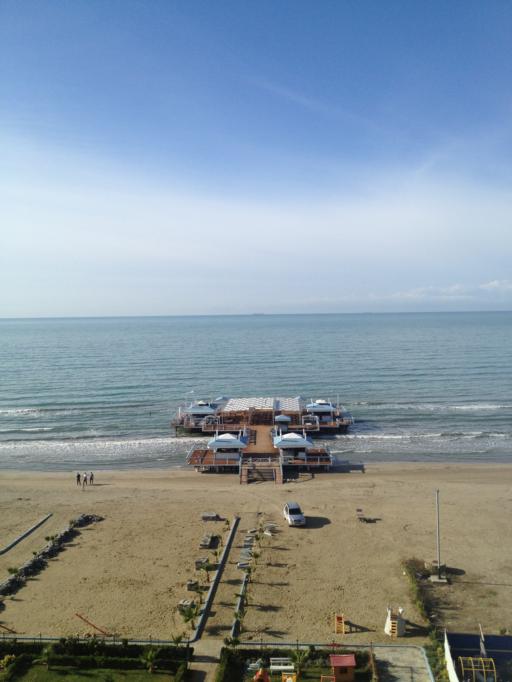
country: AL
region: Tirane
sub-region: Rrethi i Kavajes
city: Golem
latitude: 41.2809
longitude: 19.5131
